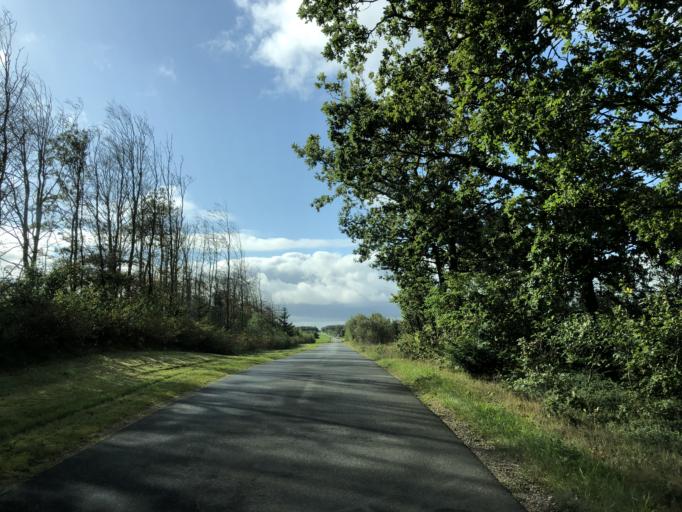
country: DK
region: Central Jutland
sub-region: Holstebro Kommune
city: Ulfborg
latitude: 56.3152
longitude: 8.4654
